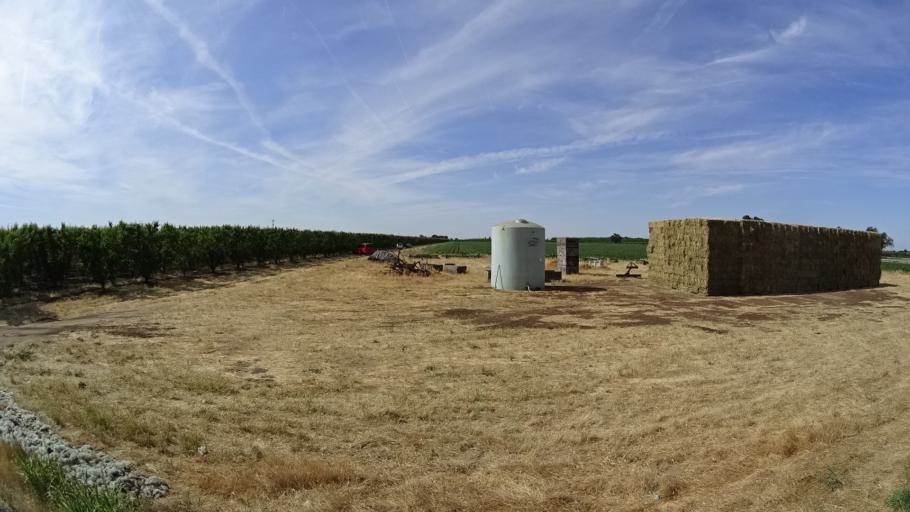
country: US
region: California
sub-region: Kings County
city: Lucerne
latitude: 36.4157
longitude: -119.6432
